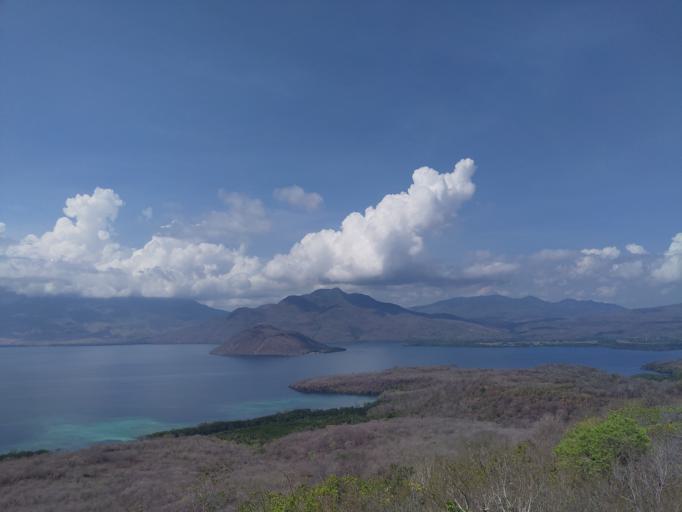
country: ID
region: East Nusa Tenggara
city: Eputobi
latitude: -8.4199
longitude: 122.8300
